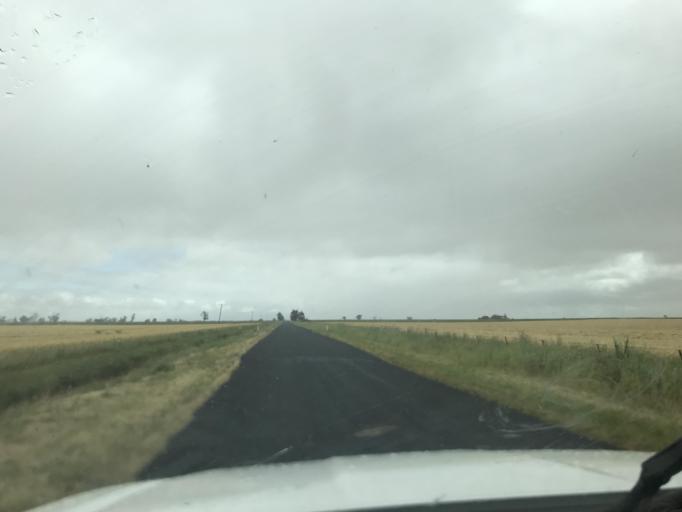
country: AU
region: South Australia
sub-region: Tatiara
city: Bordertown
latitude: -36.3015
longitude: 141.1453
